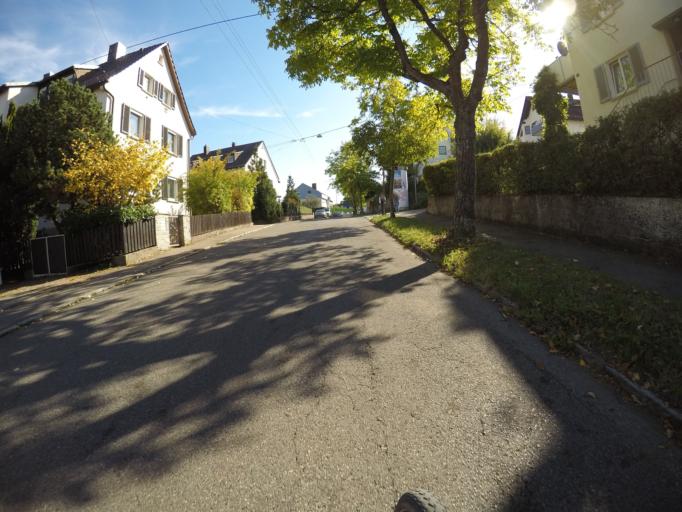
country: DE
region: Baden-Wuerttemberg
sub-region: Regierungsbezirk Stuttgart
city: Steinenbronn
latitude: 48.7206
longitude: 9.1023
